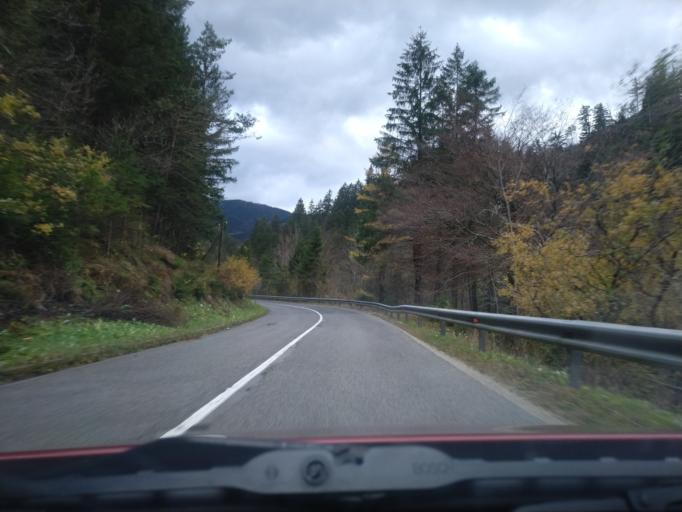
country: SI
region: Luce
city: Luce
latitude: 46.3836
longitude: 14.7248
